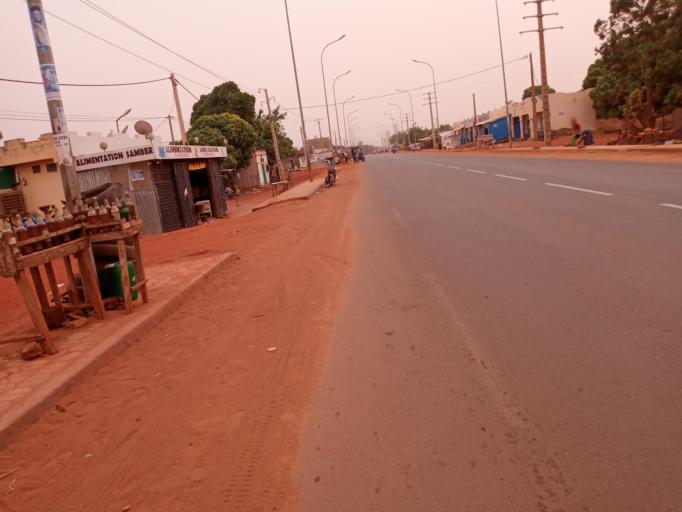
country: ML
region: Koulikoro
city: Koulikoro
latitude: 12.8459
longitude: -7.5800
